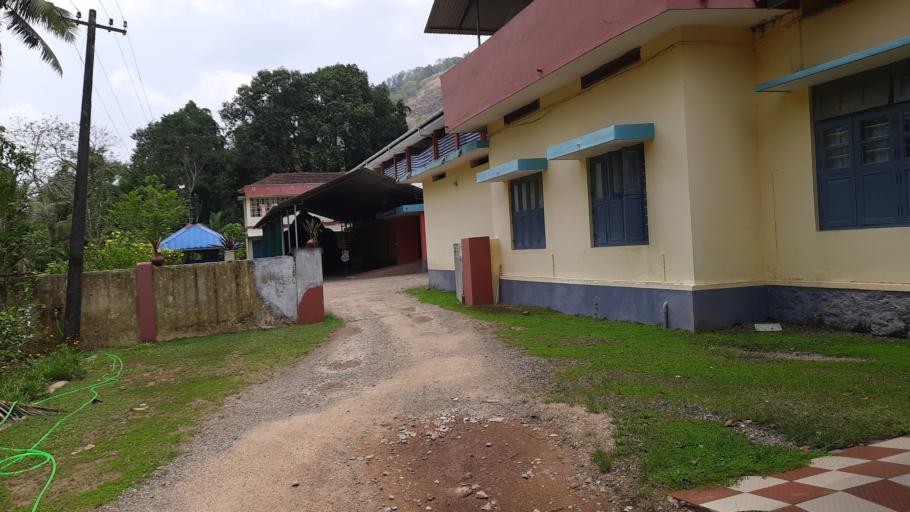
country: IN
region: Kerala
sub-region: Kottayam
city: Lalam
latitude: 9.8248
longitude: 76.7277
